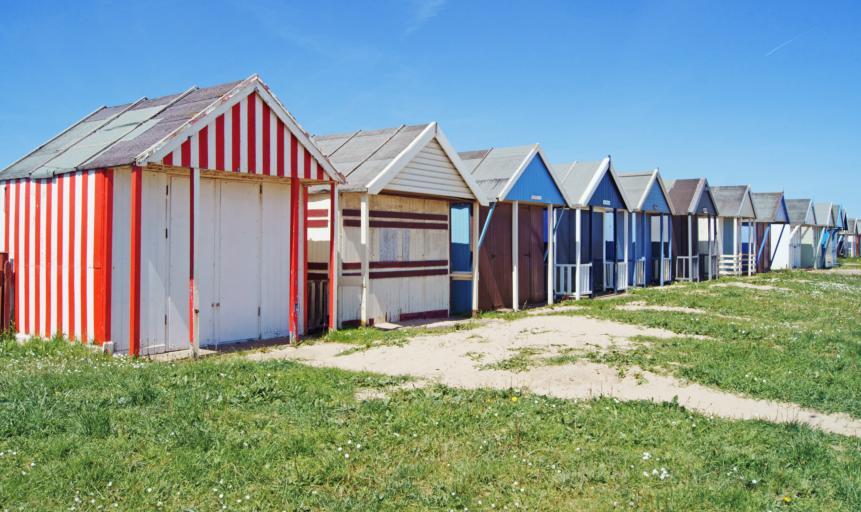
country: GB
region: England
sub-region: Lincolnshire
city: Mablethorpe
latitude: 53.3155
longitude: 0.2828
